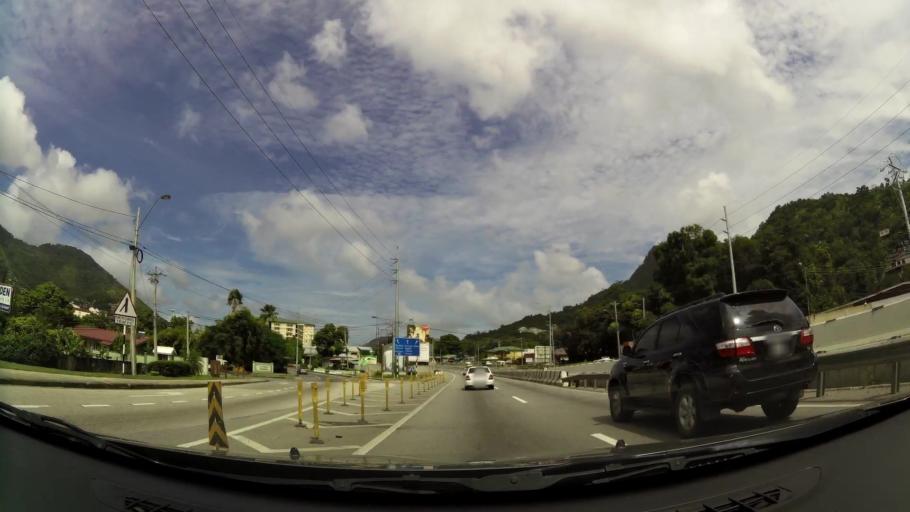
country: TT
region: Diego Martin
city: Petit Valley
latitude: 10.6838
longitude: -61.5527
